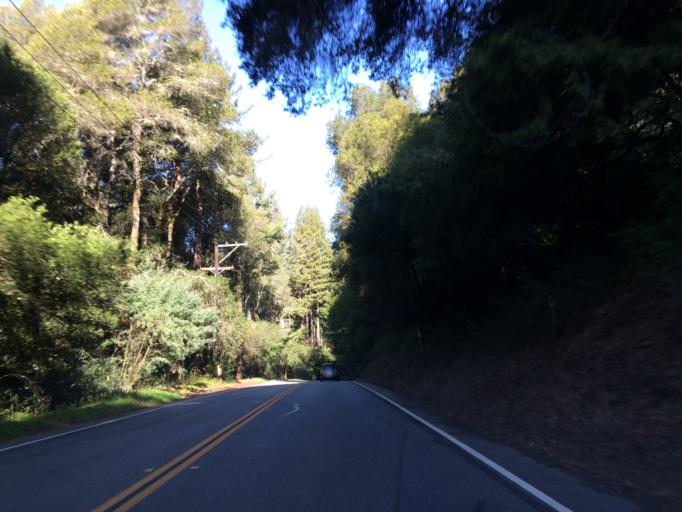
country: US
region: California
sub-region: Santa Cruz County
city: Boulder Creek
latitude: 37.1481
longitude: -122.1351
